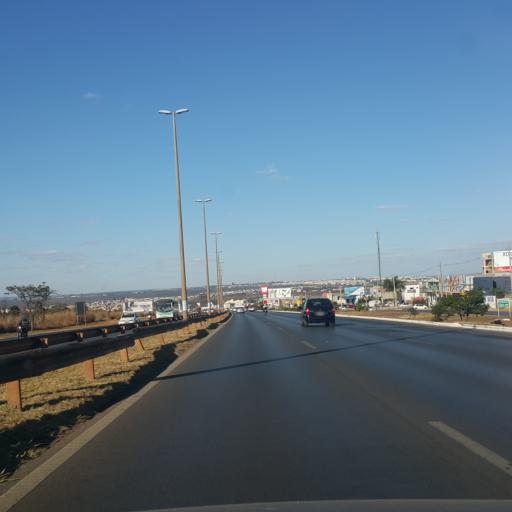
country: BR
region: Federal District
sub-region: Brasilia
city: Brasilia
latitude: -15.7909
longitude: -48.0308
